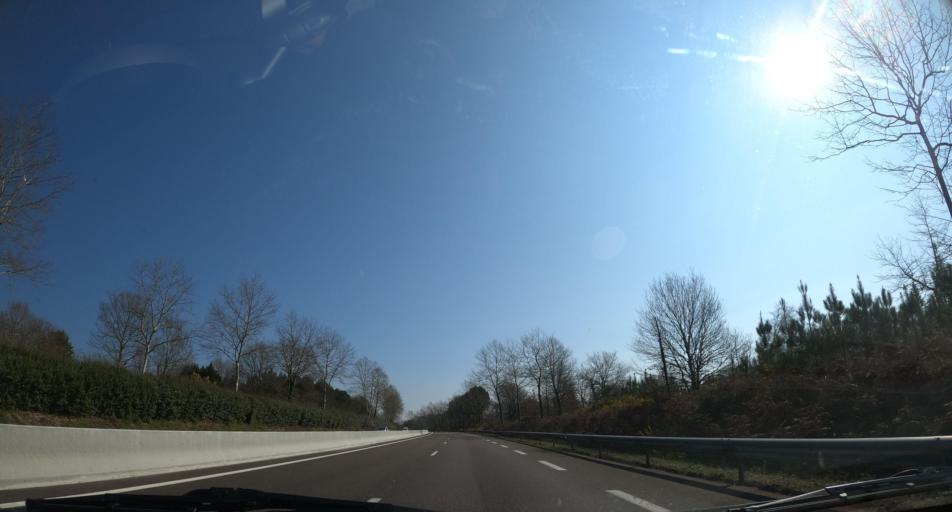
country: FR
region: Aquitaine
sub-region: Departement des Landes
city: Saint-Perdon
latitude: 43.8668
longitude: -0.6270
